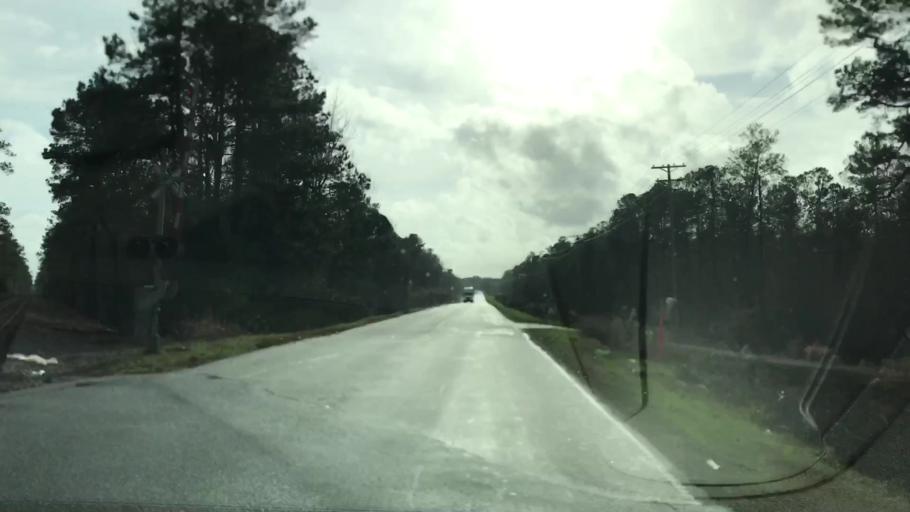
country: US
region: South Carolina
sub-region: Williamsburg County
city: Andrews
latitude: 33.4833
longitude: -79.5528
